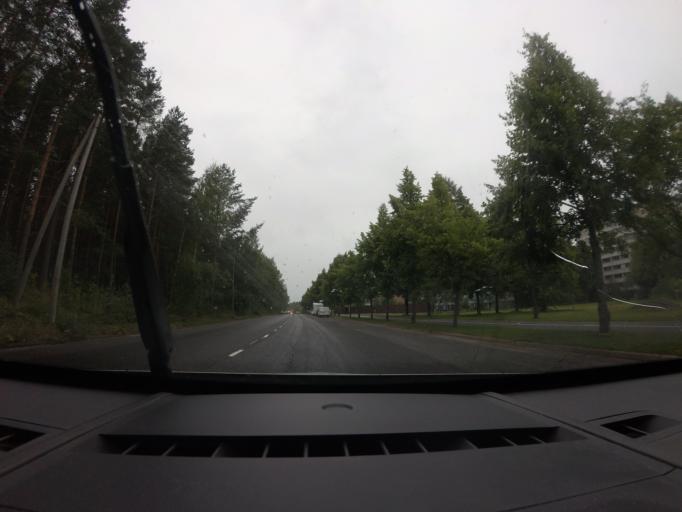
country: FI
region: Varsinais-Suomi
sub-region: Turku
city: Turku
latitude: 60.4316
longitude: 22.2846
